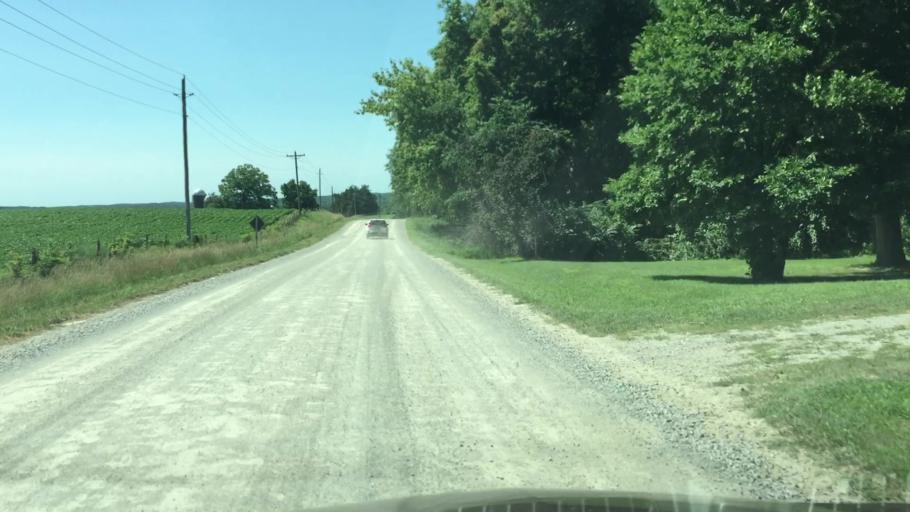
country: US
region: Iowa
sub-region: Linn County
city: Ely
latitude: 41.8322
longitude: -91.5896
